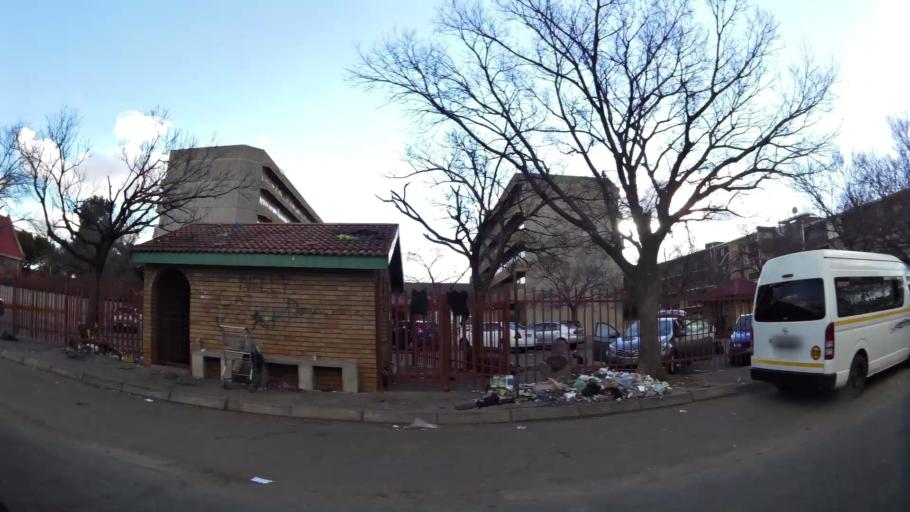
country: ZA
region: North-West
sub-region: Dr Kenneth Kaunda District Municipality
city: Potchefstroom
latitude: -26.7121
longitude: 27.0962
